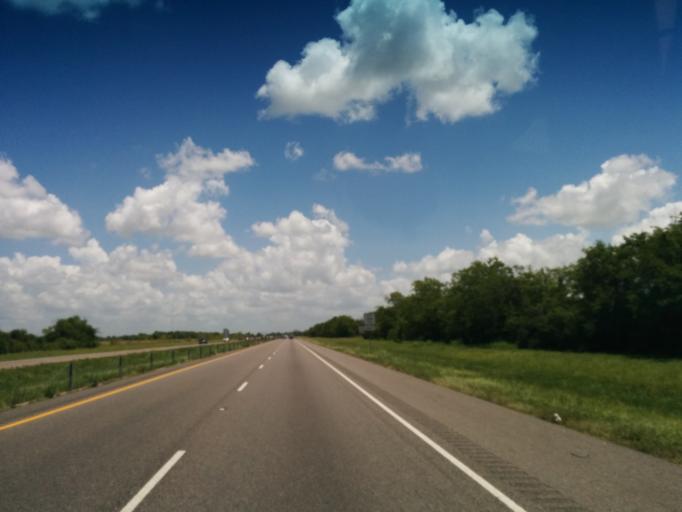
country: US
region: Texas
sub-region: Jefferson County
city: Fannett
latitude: 29.9391
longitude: -94.2595
